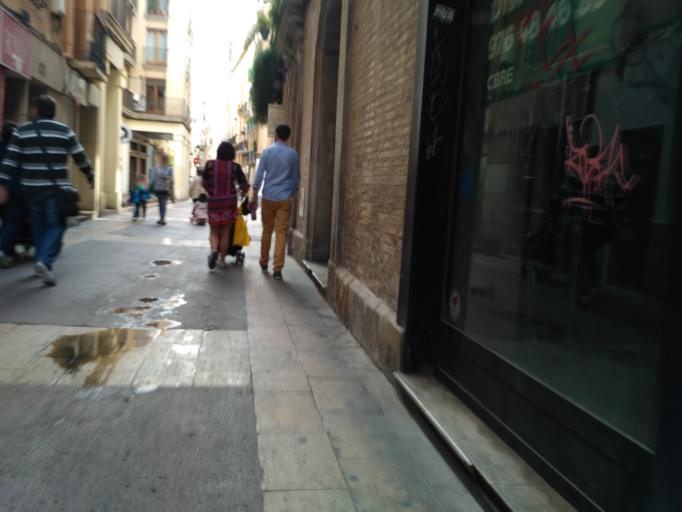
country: ES
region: Aragon
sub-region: Provincia de Zaragoza
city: Zaragoza
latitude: 41.6536
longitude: -0.8793
